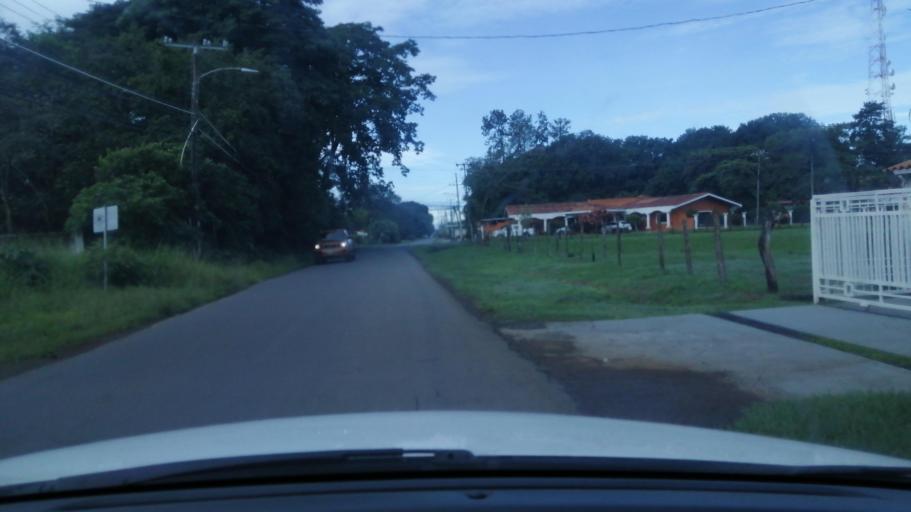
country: PA
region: Chiriqui
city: Mata del Nance
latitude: 8.4571
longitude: -82.4186
